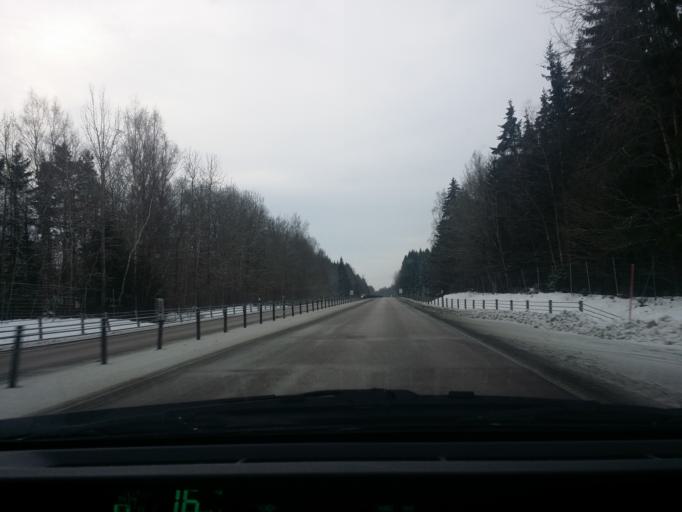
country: SE
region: Vaestra Goetaland
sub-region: Mariestads Kommun
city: Mariestad
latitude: 58.6070
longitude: 13.8026
